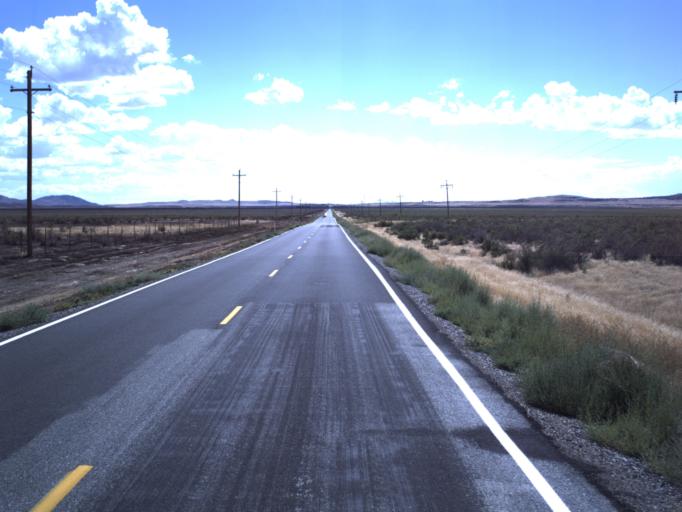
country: US
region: Utah
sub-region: Tooele County
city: Grantsville
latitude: 40.2827
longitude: -112.6683
